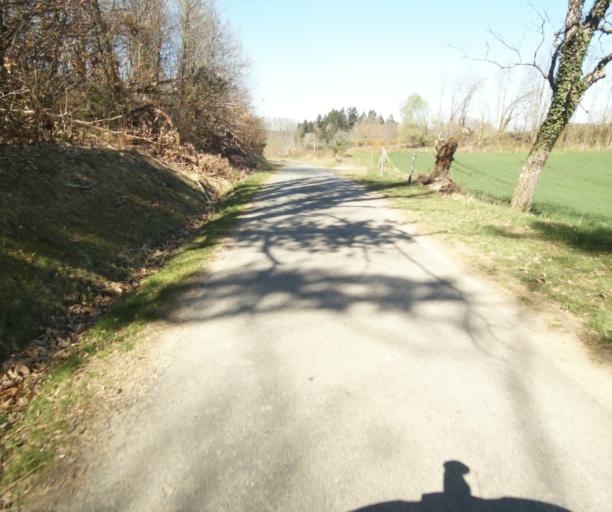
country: FR
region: Limousin
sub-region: Departement de la Correze
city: Saint-Mexant
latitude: 45.2925
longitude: 1.6421
